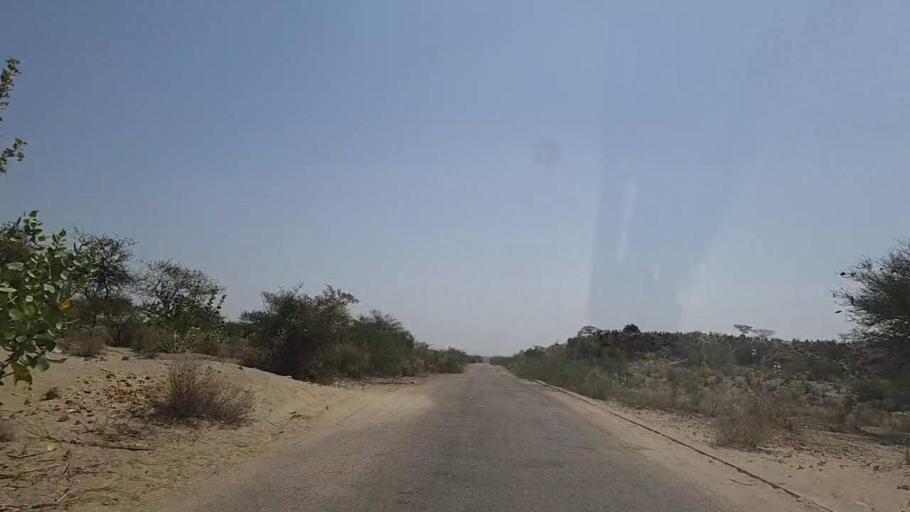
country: PK
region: Sindh
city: Diplo
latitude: 24.5044
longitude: 69.4259
